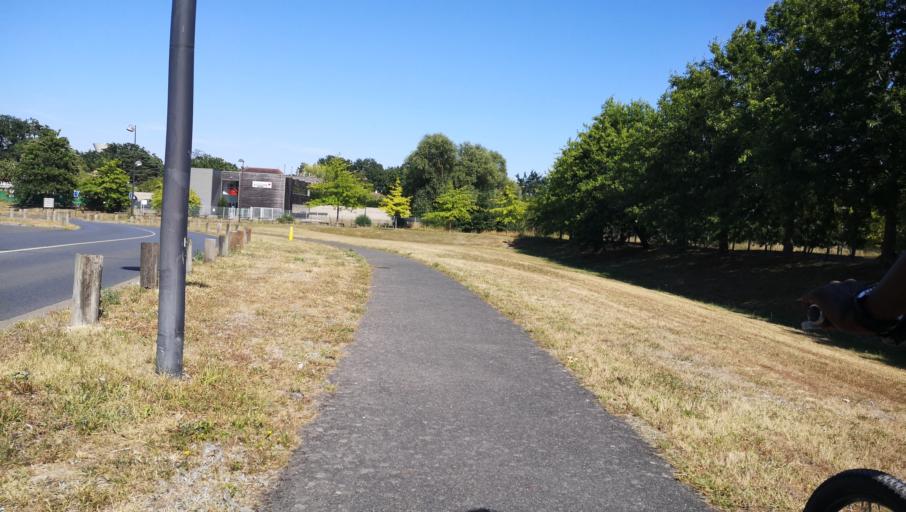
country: FR
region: Centre
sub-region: Departement du Loiret
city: Boigny-sur-Bionne
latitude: 47.9230
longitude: 1.9995
